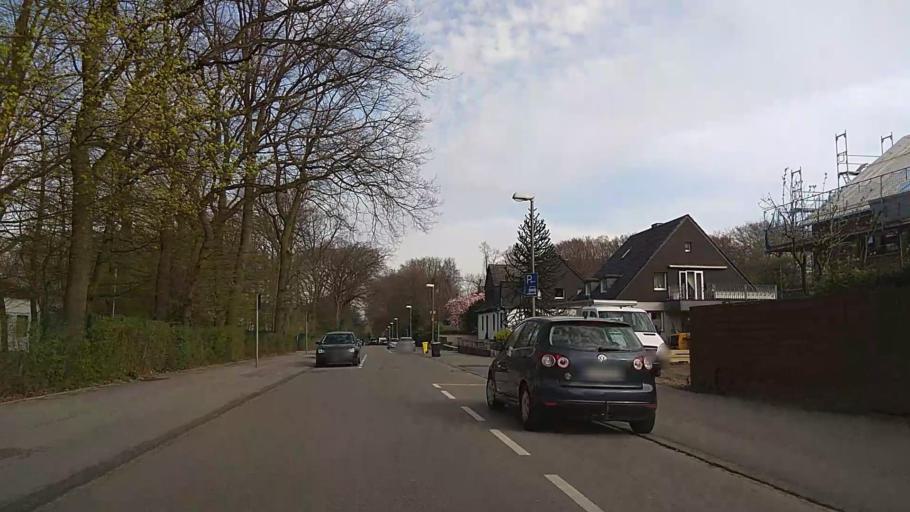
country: DE
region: North Rhine-Westphalia
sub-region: Regierungsbezirk Munster
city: Gladbeck
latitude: 51.5768
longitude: 7.0391
